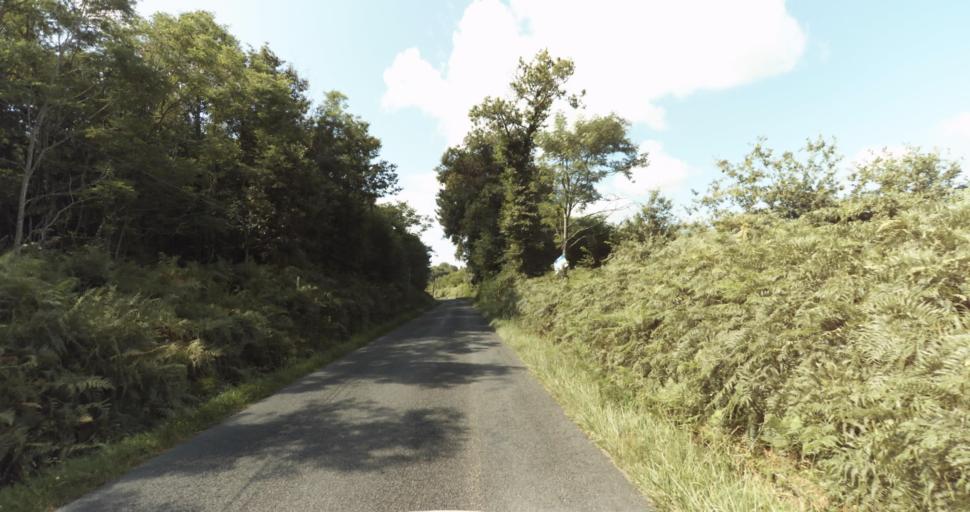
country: FR
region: Aquitaine
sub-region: Departement de la Gironde
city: Bazas
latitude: 44.4560
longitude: -0.2064
